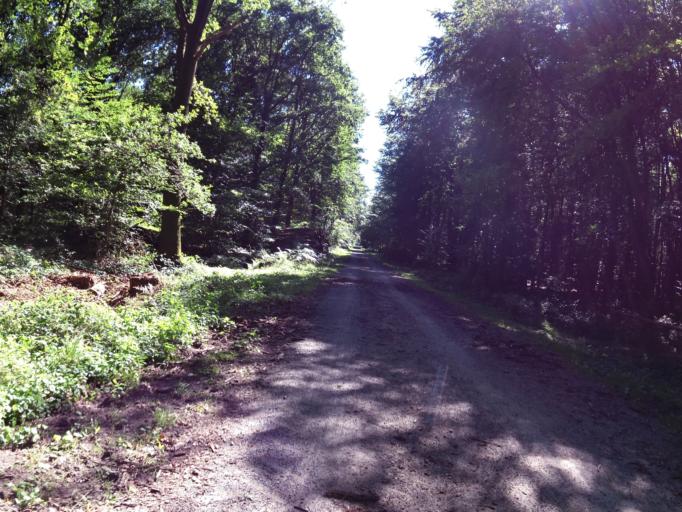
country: DE
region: North Rhine-Westphalia
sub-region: Regierungsbezirk Dusseldorf
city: Kranenburg
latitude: 51.7615
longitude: 5.9996
